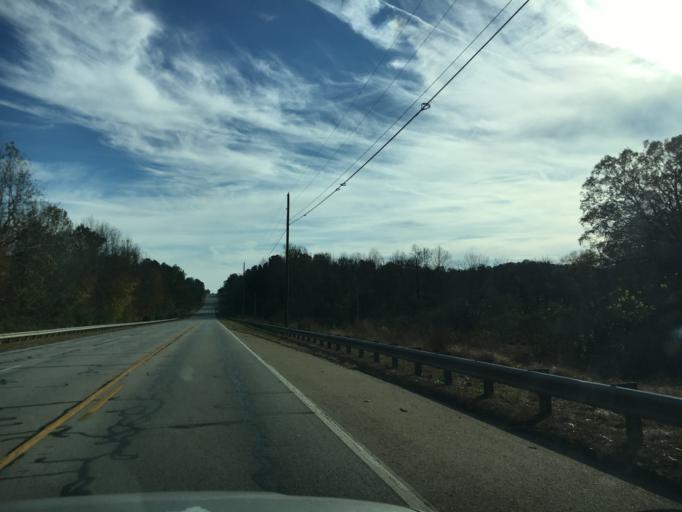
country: US
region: Georgia
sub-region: Elbert County
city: Elberton
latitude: 34.1450
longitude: -82.8617
